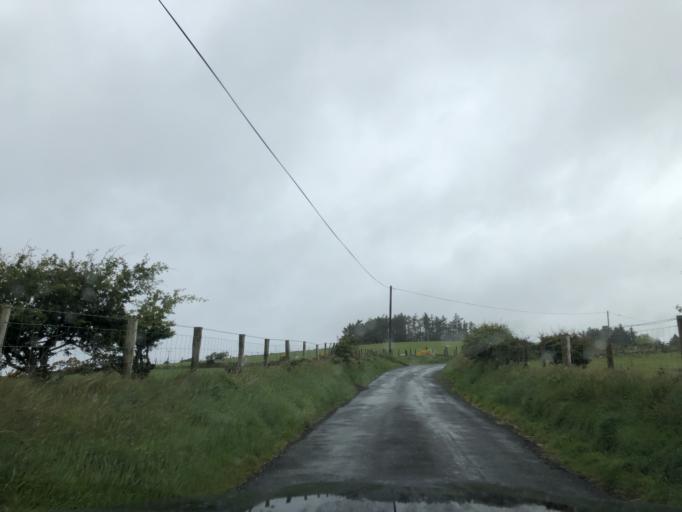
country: GB
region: Northern Ireland
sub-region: Moyle District
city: Ballycastle
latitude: 55.2051
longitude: -6.1717
